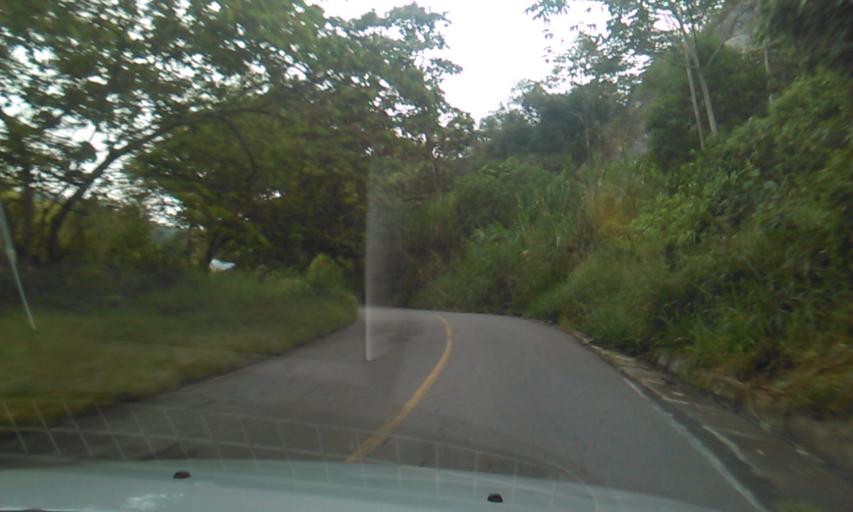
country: CO
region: Quindio
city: Cordoba
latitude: 4.4067
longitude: -75.7048
